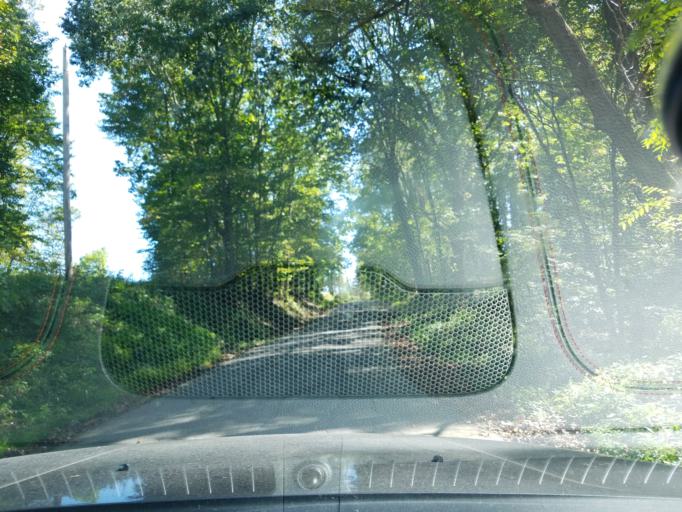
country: US
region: Pennsylvania
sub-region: Lawrence County
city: Ellwood City
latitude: 40.9333
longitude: -80.3119
